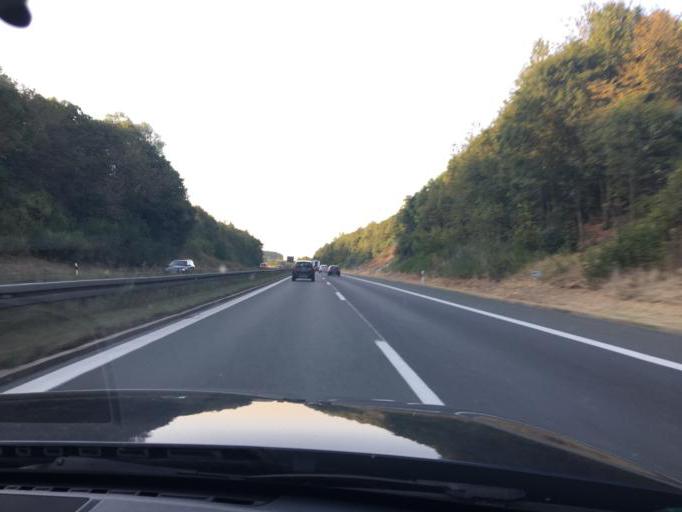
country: DE
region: Bavaria
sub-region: Upper Franconia
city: Hirschaid
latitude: 49.8363
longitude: 11.0044
